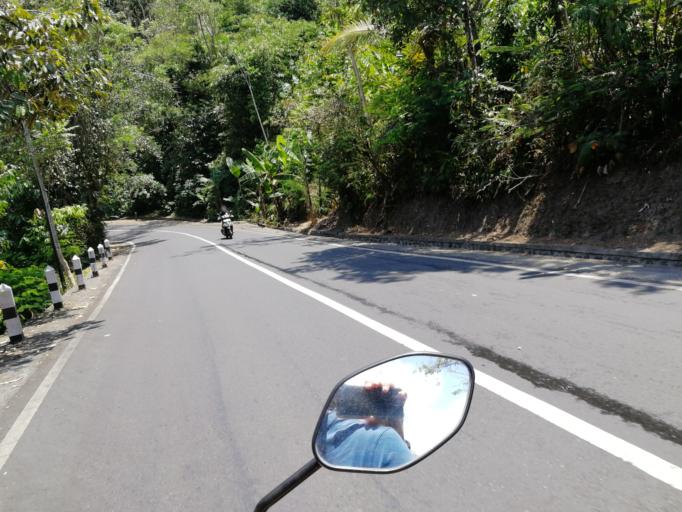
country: ID
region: Bali
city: Banjar Kubu
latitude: -8.4486
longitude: 115.3883
